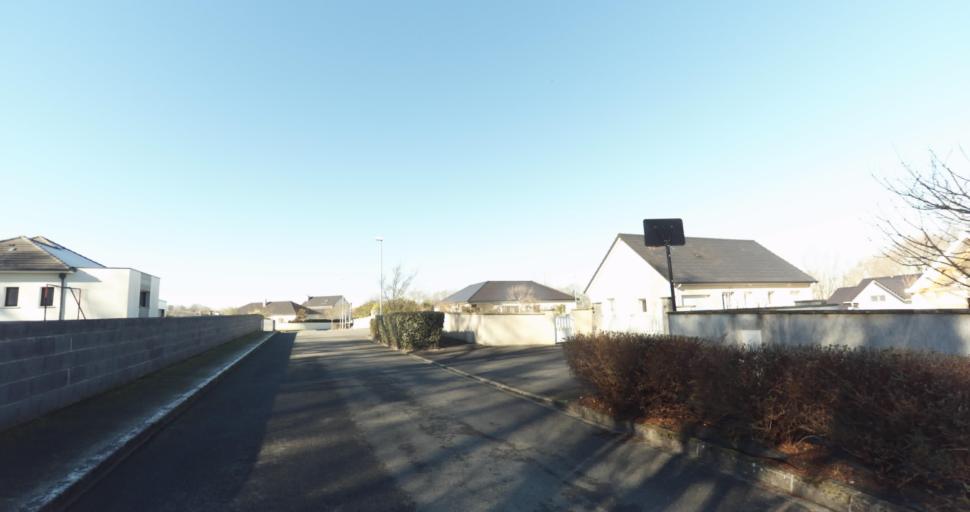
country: FR
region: Aquitaine
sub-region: Departement des Pyrenees-Atlantiques
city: Morlaas
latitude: 43.3574
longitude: -0.2665
